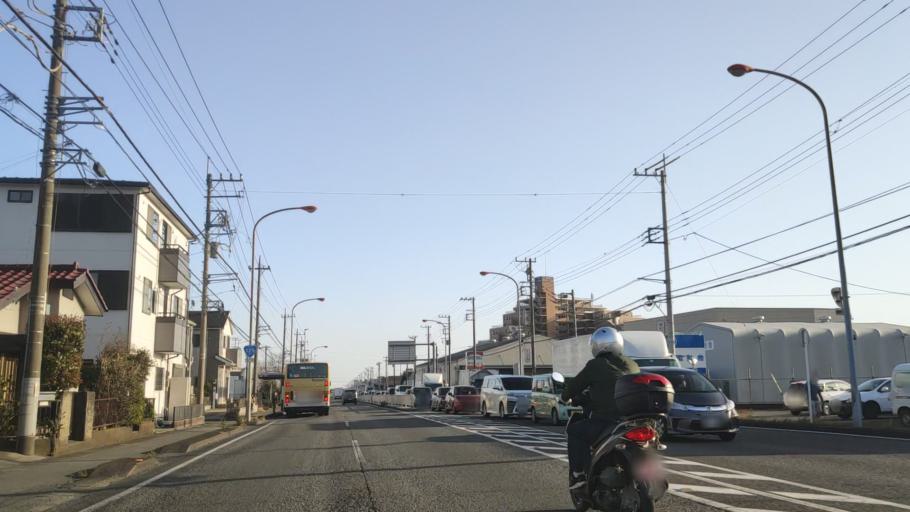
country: JP
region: Kanagawa
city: Zama
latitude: 35.4852
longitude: 139.3652
